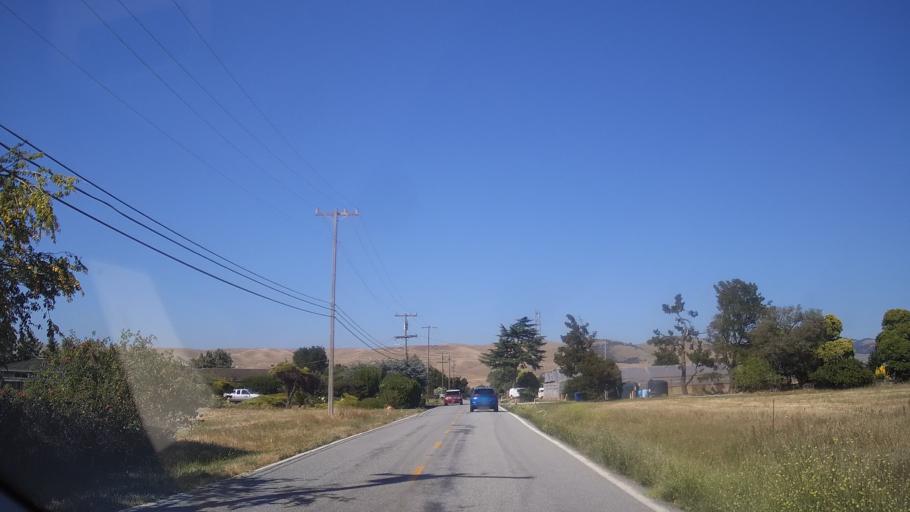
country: US
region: California
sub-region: Santa Clara County
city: Morgan Hill
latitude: 37.1620
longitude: -121.6971
